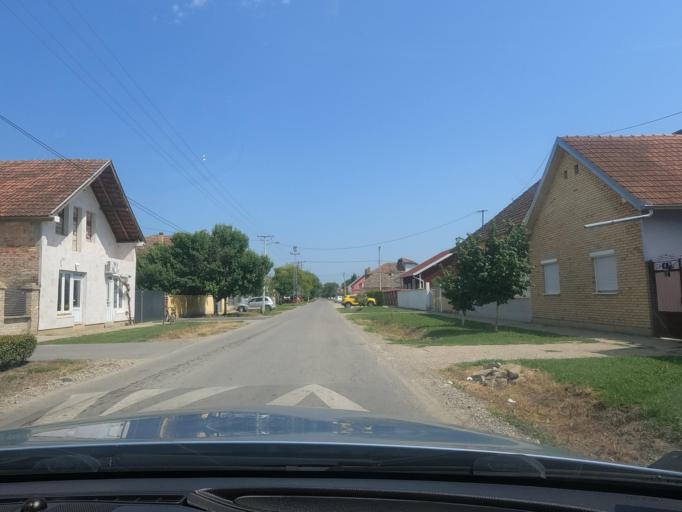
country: RS
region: Autonomna Pokrajina Vojvodina
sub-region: Juznobacki Okrug
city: Kovilj
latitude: 45.2239
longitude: 20.0234
